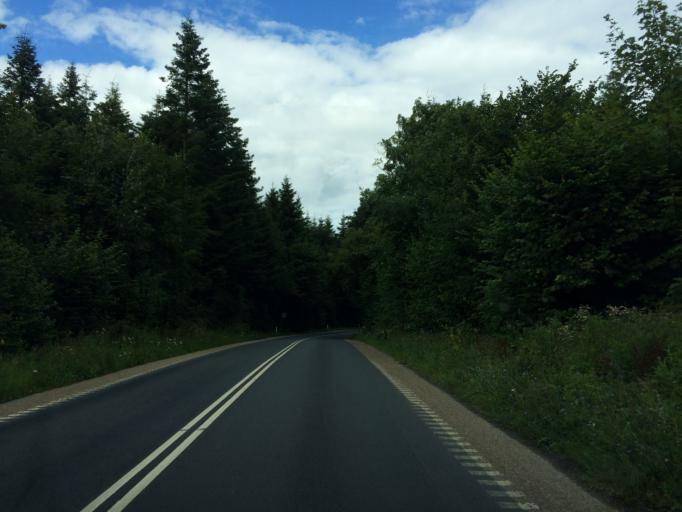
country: DK
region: South Denmark
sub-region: Assens Kommune
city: Harby
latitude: 55.1662
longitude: 10.1421
